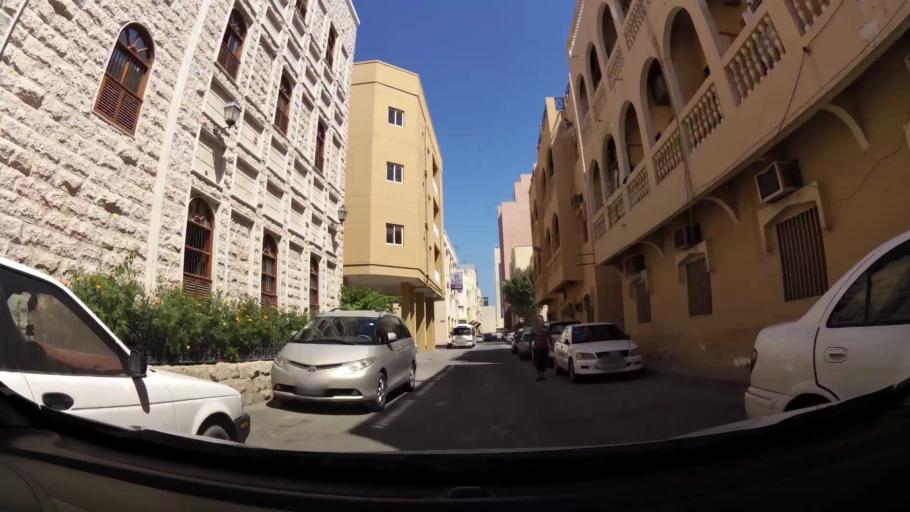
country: BH
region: Manama
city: Manama
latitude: 26.2004
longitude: 50.5948
